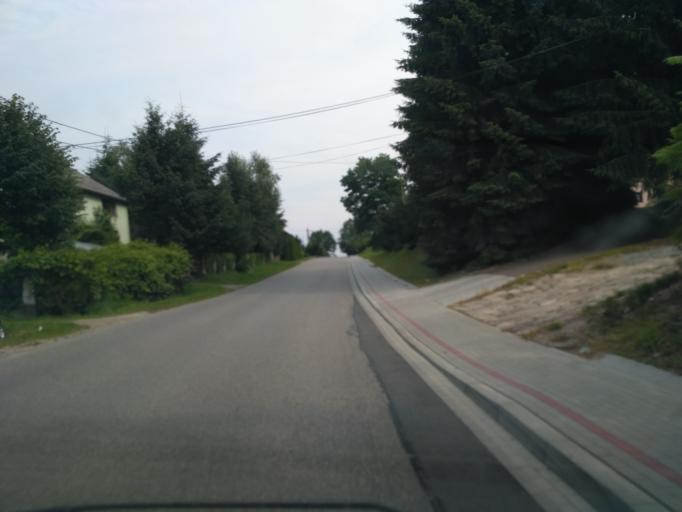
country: PL
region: Subcarpathian Voivodeship
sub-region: Powiat strzyzowski
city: Niebylec
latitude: 49.8539
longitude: 21.9116
